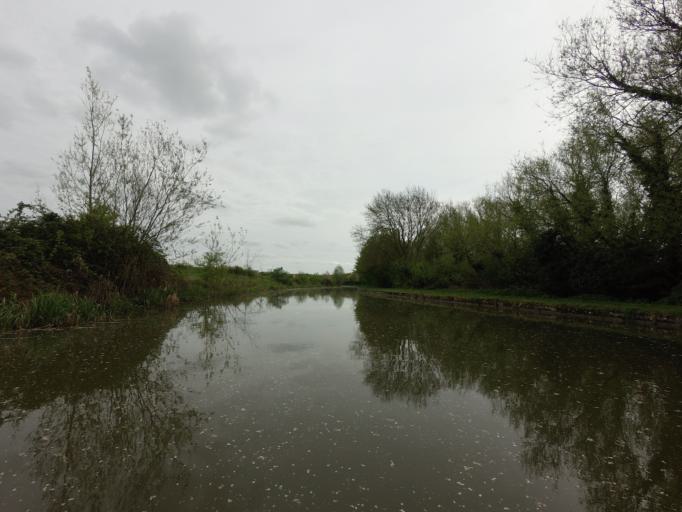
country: GB
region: England
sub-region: Milton Keynes
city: Bradwell
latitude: 52.0731
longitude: -0.7819
